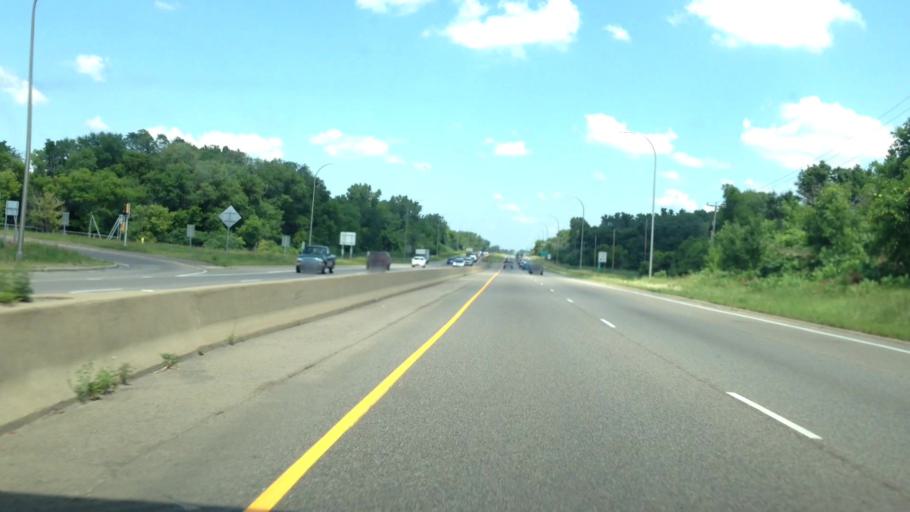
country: US
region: Minnesota
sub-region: Hennepin County
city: New Hope
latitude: 45.0694
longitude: -93.4011
